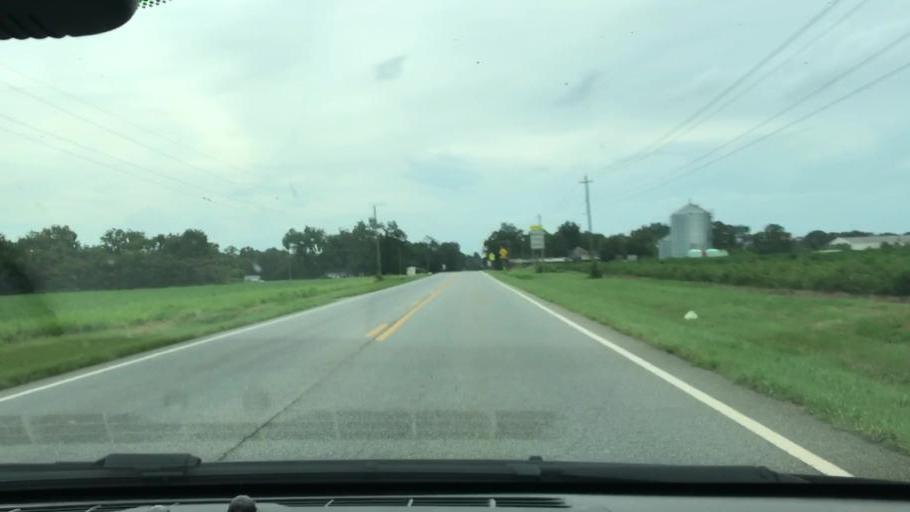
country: US
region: Georgia
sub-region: Early County
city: Blakely
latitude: 31.3776
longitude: -84.9575
